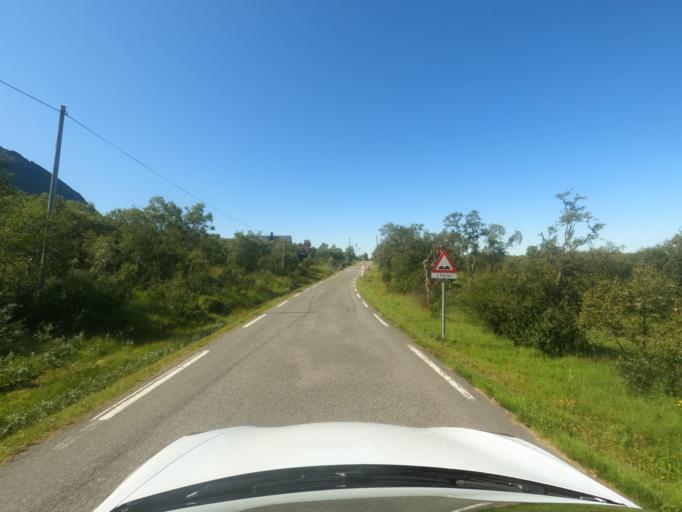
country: NO
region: Nordland
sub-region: Hadsel
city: Melbu
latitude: 68.4337
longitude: 14.7593
